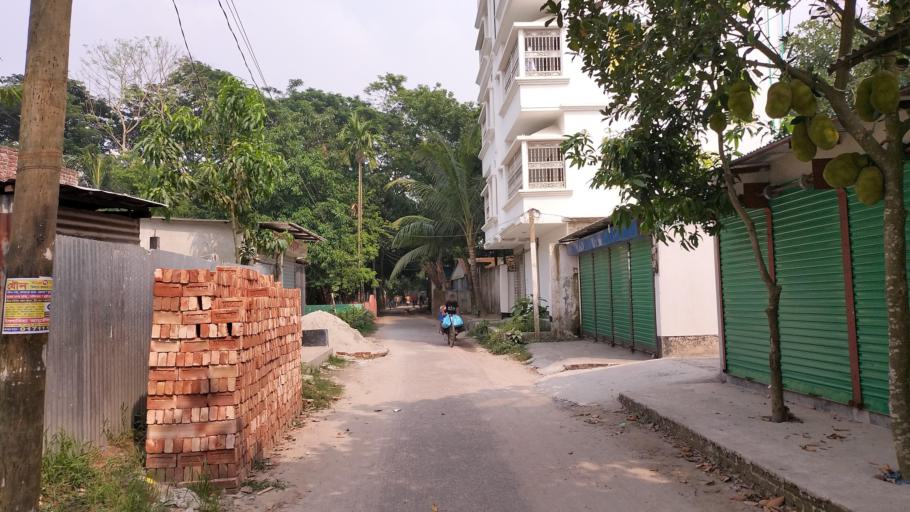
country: BD
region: Dhaka
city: Azimpur
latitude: 23.6905
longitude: 90.3009
